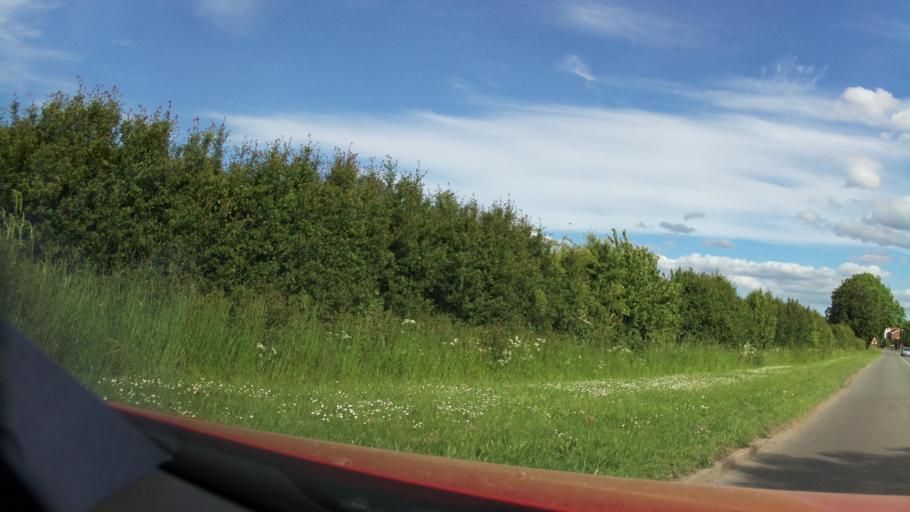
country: GB
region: England
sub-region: Worcestershire
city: Badsey
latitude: 52.0867
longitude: -1.8587
